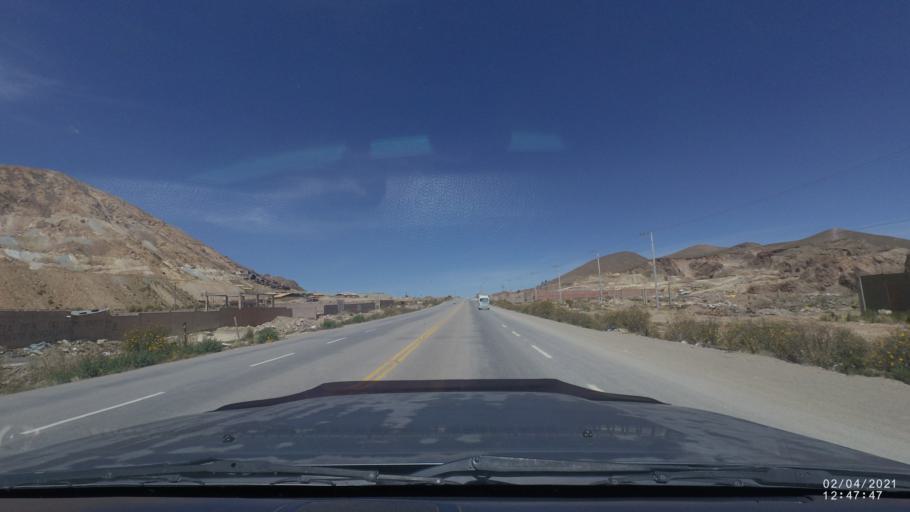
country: BO
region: Oruro
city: Oruro
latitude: -17.9570
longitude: -67.1432
